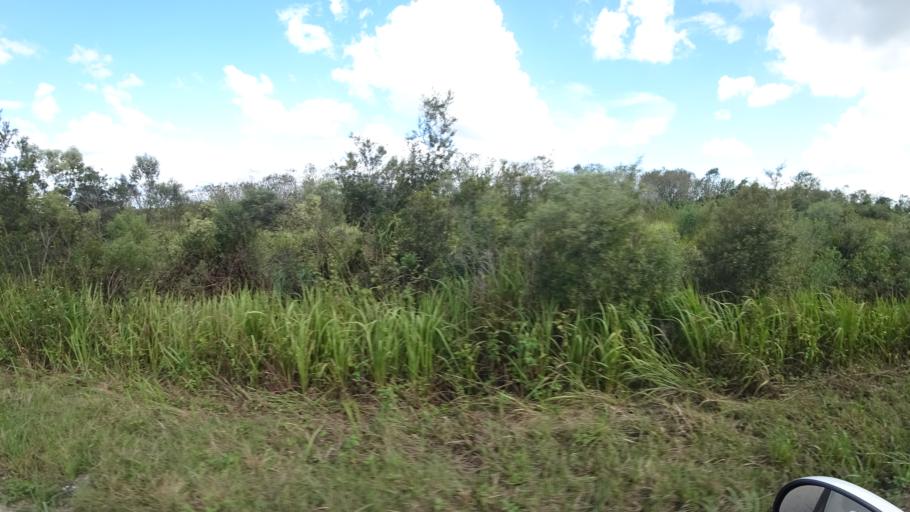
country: US
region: Florida
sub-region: DeSoto County
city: Arcadia
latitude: 27.3387
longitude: -82.1050
